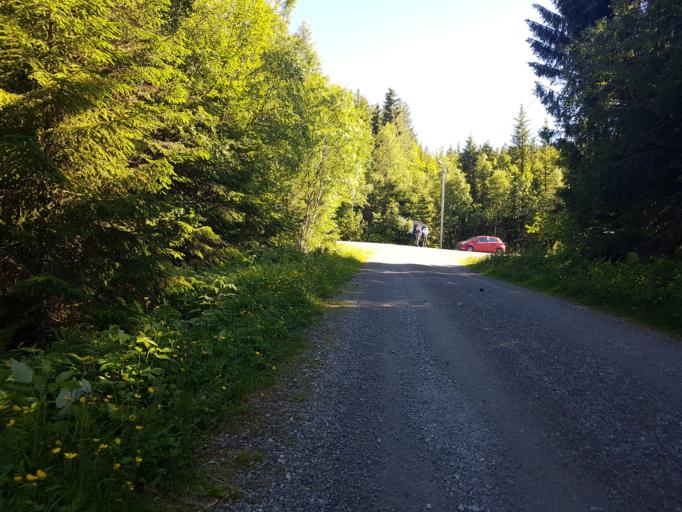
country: NO
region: Sor-Trondelag
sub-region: Trondheim
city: Trondheim
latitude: 63.4339
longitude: 10.2728
